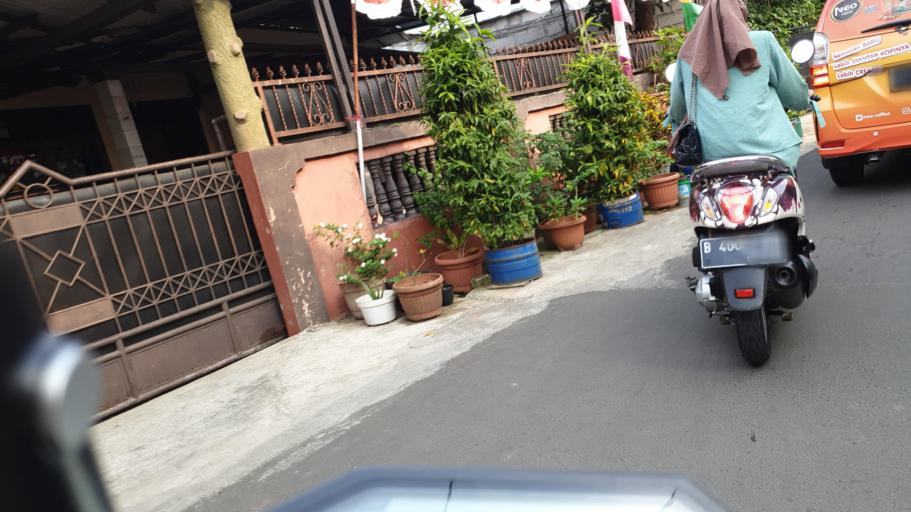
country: ID
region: West Java
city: Depok
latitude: -6.3391
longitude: 106.8317
